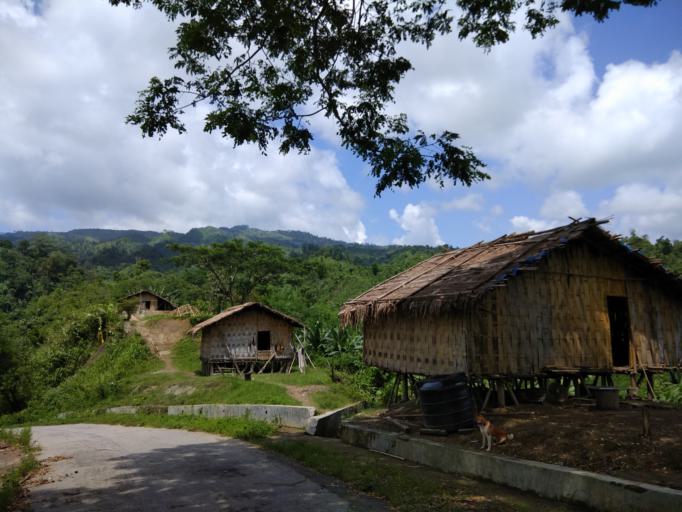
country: BD
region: Chittagong
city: Satkania
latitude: 21.7206
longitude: 92.3874
